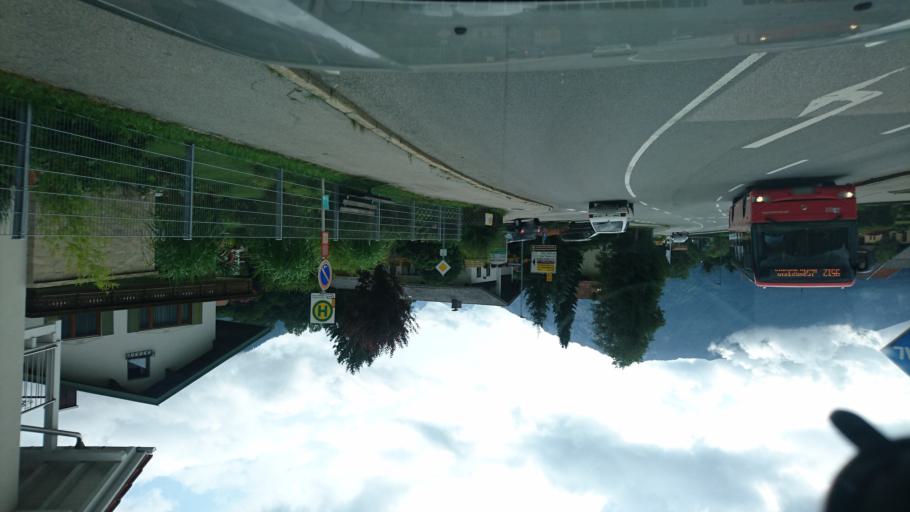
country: DE
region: Bavaria
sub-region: Upper Bavaria
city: Ruhpolding
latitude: 47.7662
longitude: 12.6405
